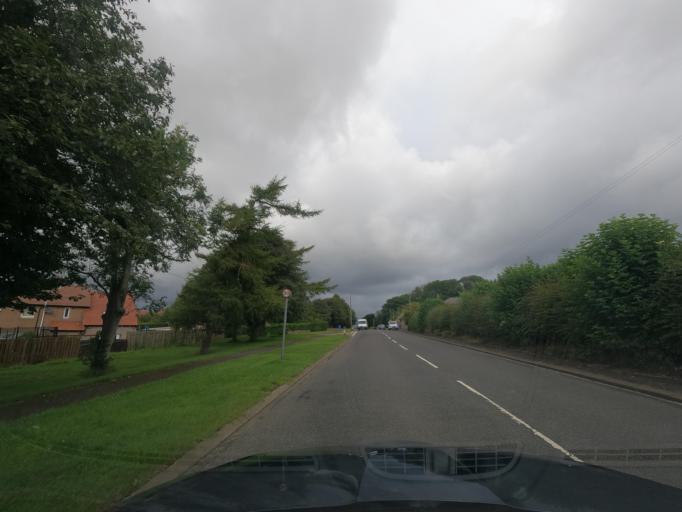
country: GB
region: England
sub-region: Northumberland
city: Ancroft
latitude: 55.7345
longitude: -1.9899
